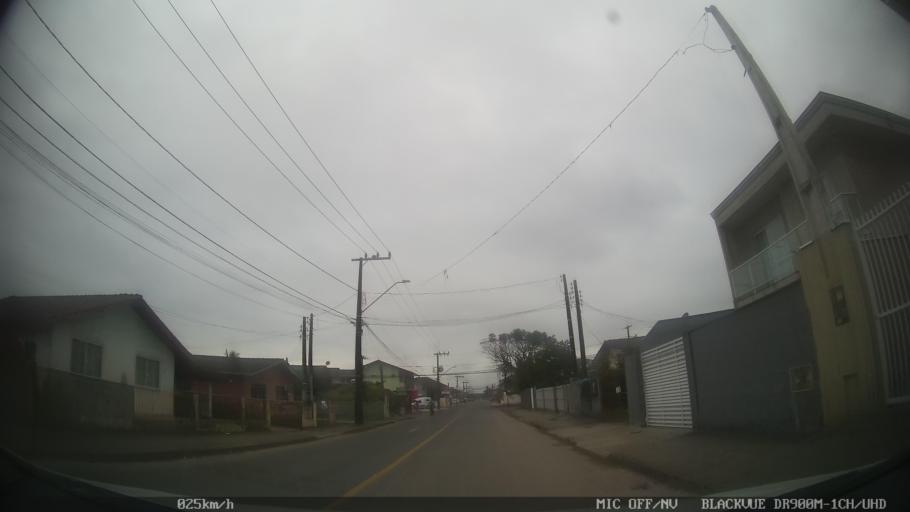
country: BR
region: Santa Catarina
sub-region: Joinville
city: Joinville
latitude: -26.3206
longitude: -48.8185
